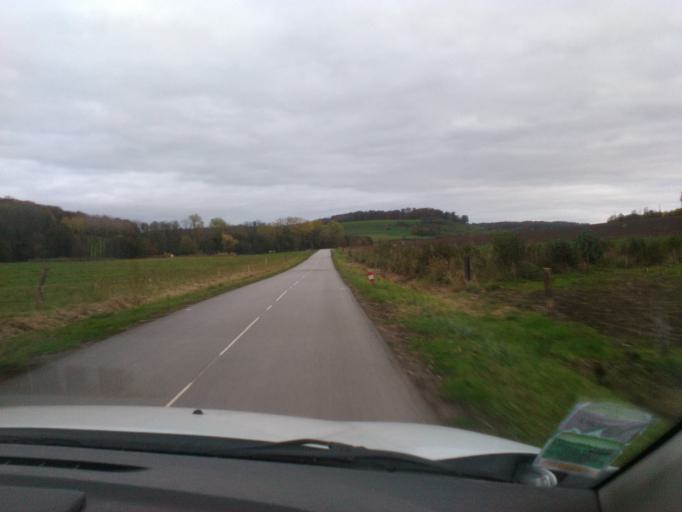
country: FR
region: Lorraine
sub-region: Departement des Vosges
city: Vincey
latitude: 48.2740
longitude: 6.2480
